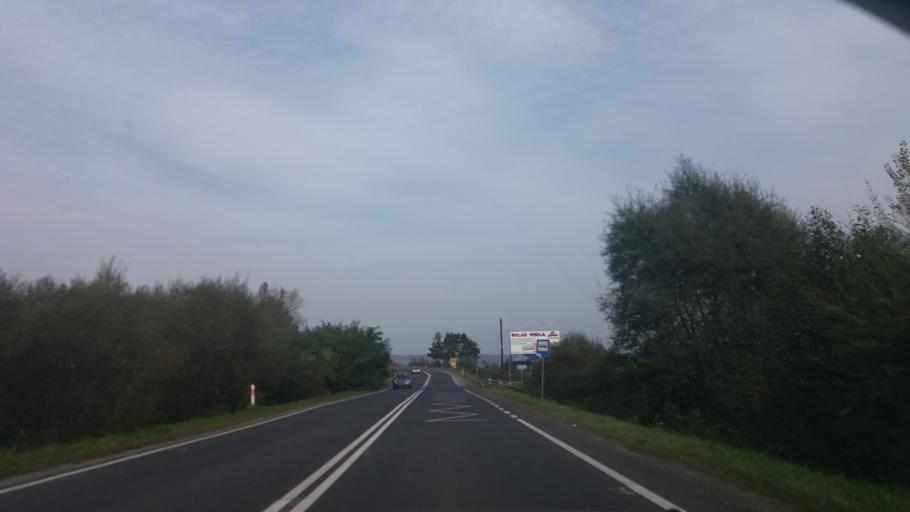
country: PL
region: Lesser Poland Voivodeship
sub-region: Powiat oswiecimski
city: Zator
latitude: 50.0253
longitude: 19.4360
